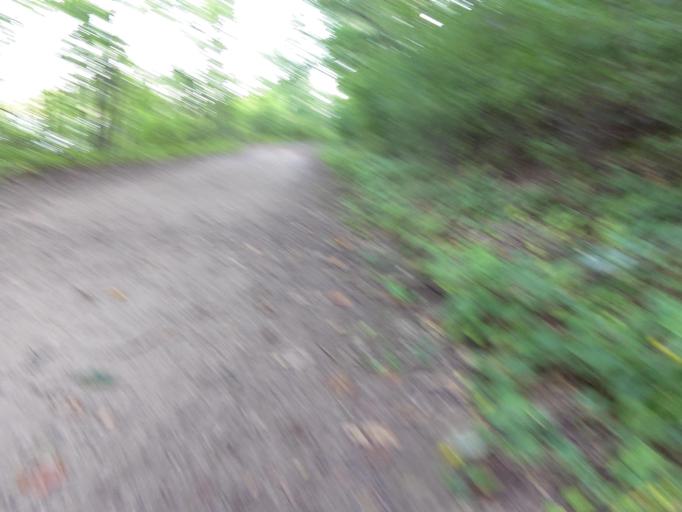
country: US
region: Minnesota
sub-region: Washington County
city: Afton
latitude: 44.8574
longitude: -92.7733
